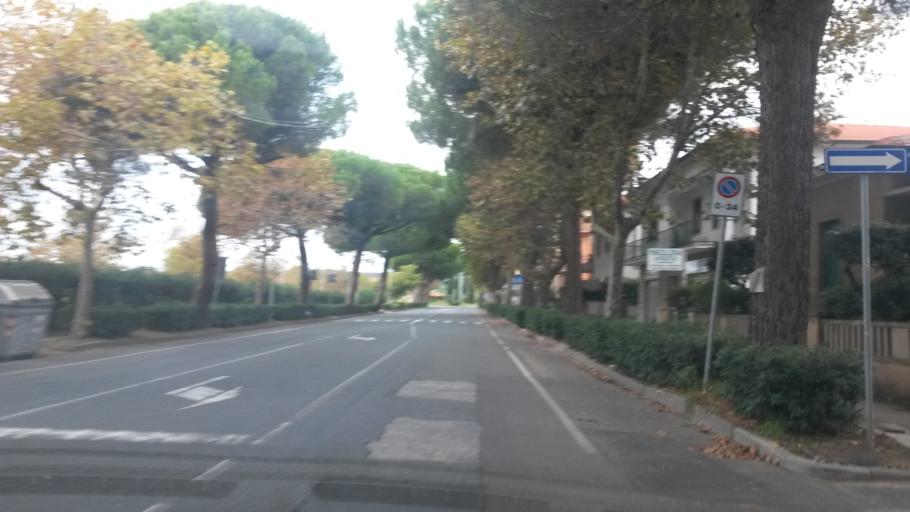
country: IT
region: Tuscany
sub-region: Provincia di Livorno
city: Rosignano Solvay-Castiglioncello
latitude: 43.3956
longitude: 10.4366
